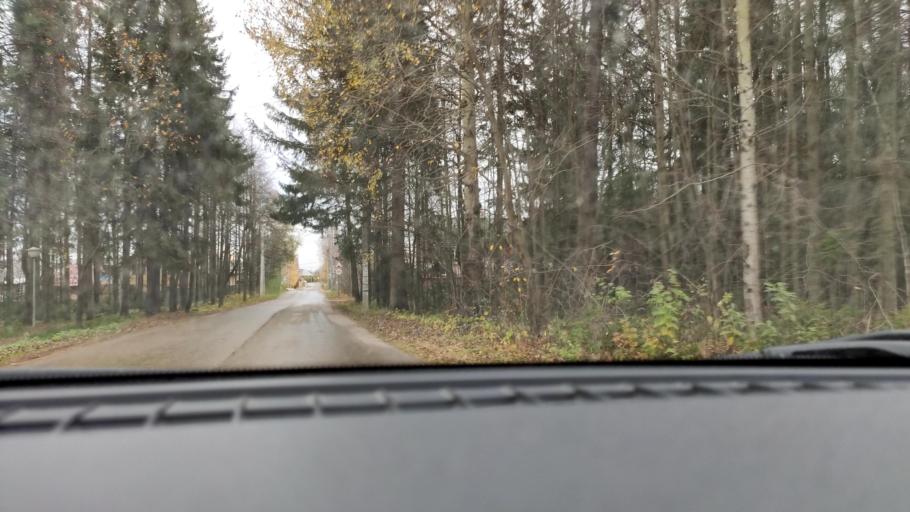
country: RU
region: Perm
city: Froly
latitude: 57.9533
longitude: 56.3007
